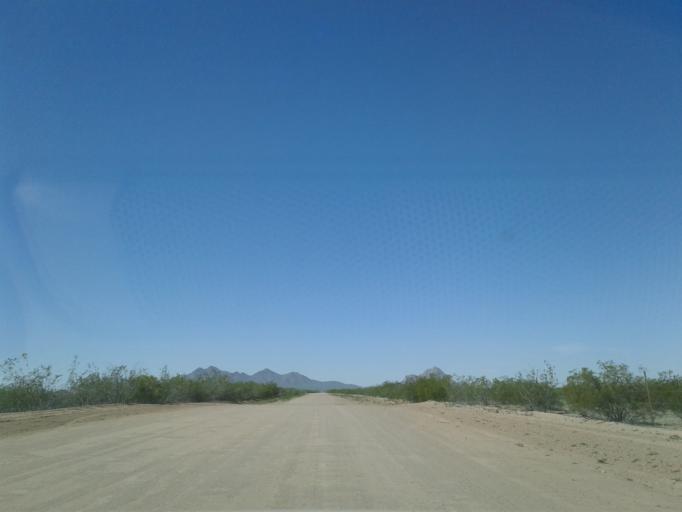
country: US
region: Arizona
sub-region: Pima County
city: Avra Valley
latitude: 32.4294
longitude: -111.3498
